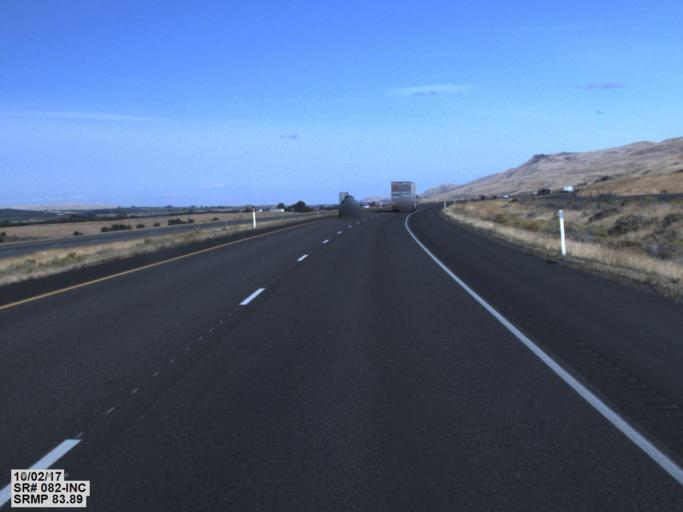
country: US
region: Washington
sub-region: Benton County
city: Prosser
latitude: 46.2185
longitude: -119.7174
